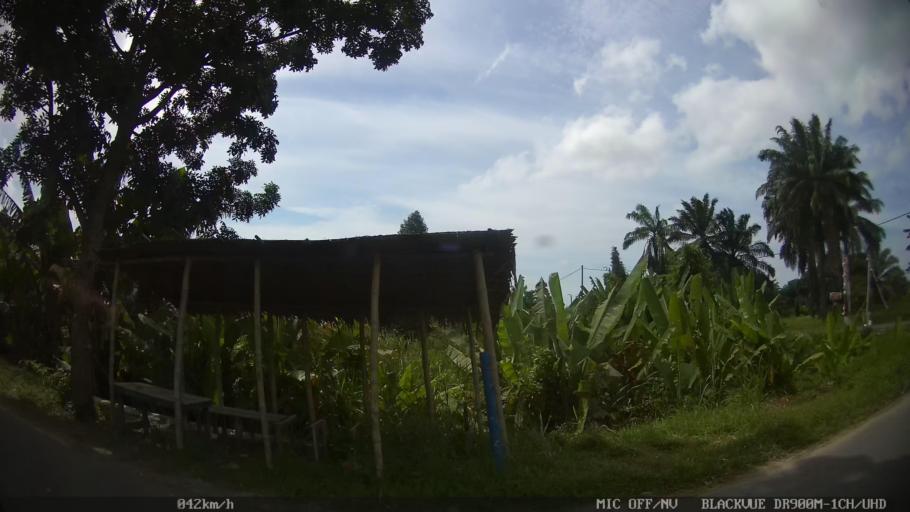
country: ID
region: North Sumatra
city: Percut
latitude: 3.6084
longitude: 98.8432
